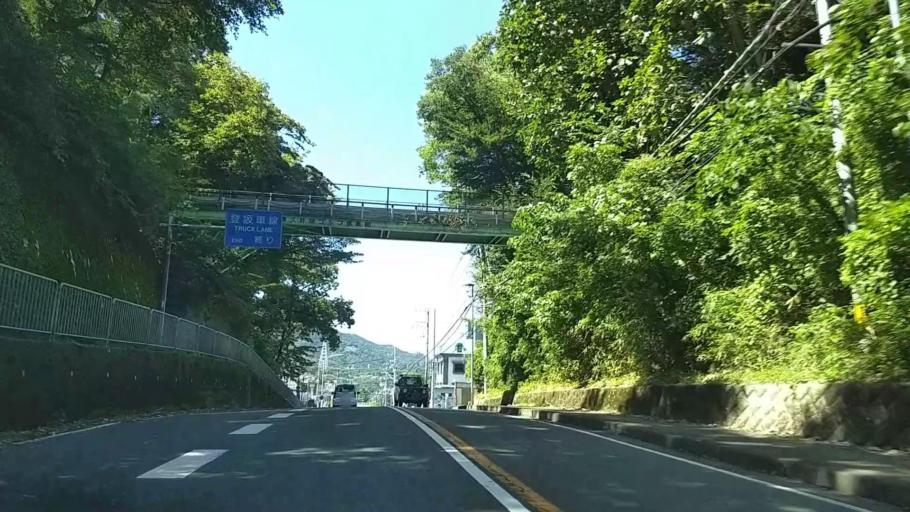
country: JP
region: Tokyo
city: Hachioji
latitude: 35.5878
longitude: 139.2369
